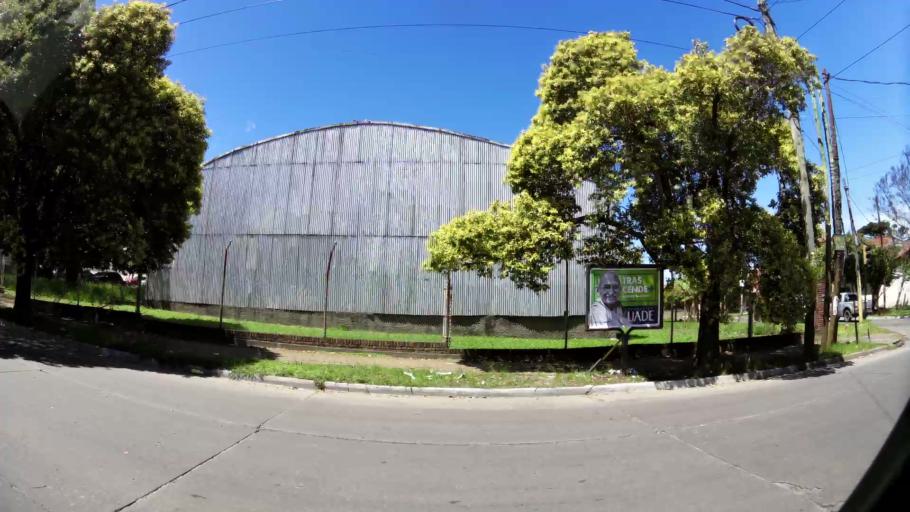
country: AR
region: Buenos Aires
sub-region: Partido de Quilmes
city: Quilmes
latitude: -34.7386
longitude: -58.2817
